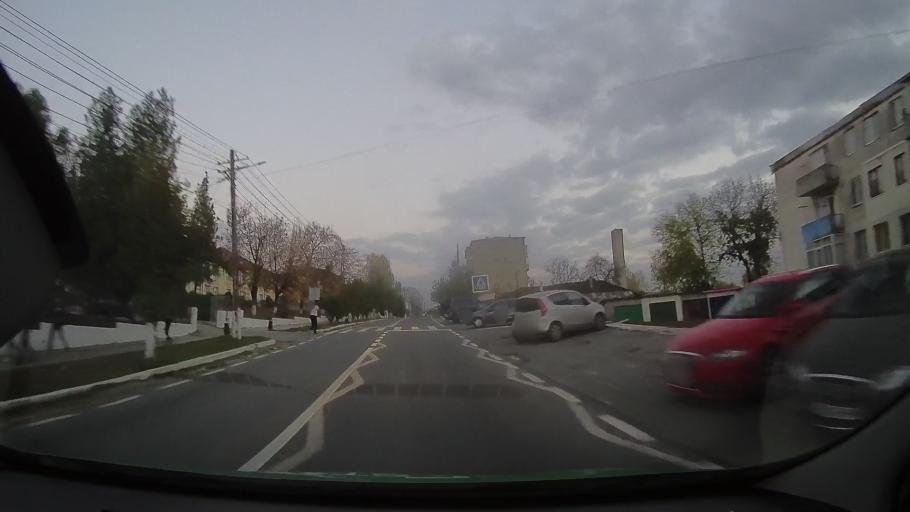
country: RO
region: Constanta
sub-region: Comuna Baneasa
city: Baneasa
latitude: 44.0666
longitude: 27.6959
